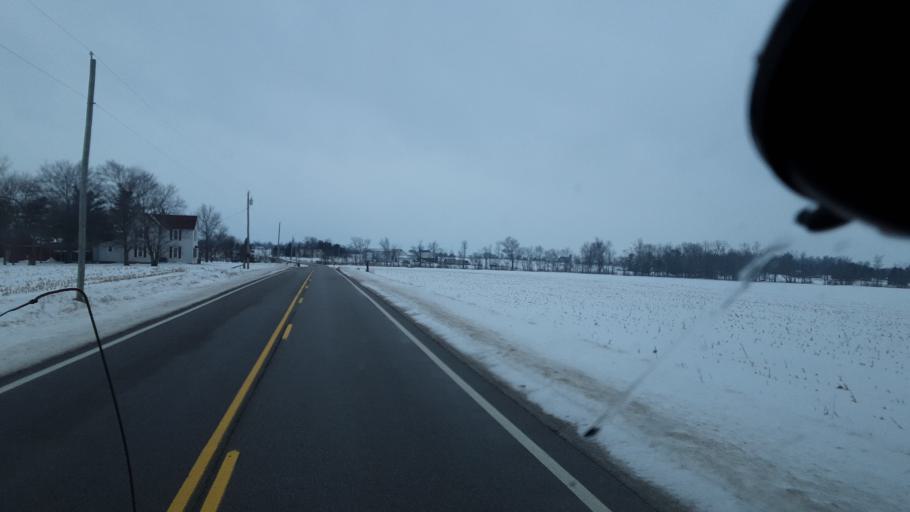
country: US
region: Ohio
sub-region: Union County
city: Marysville
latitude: 40.1705
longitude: -83.3449
